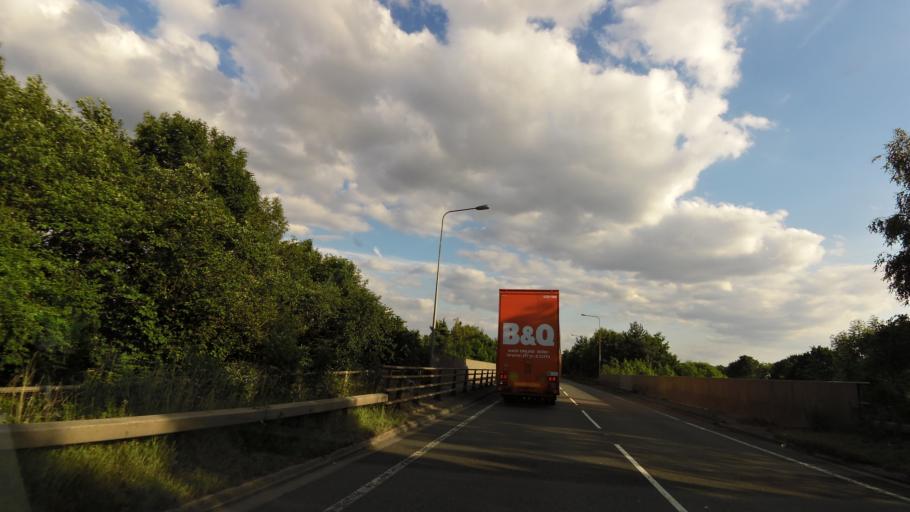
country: GB
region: England
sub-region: Rotherham
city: Woodsetts
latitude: 53.3210
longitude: -1.1536
